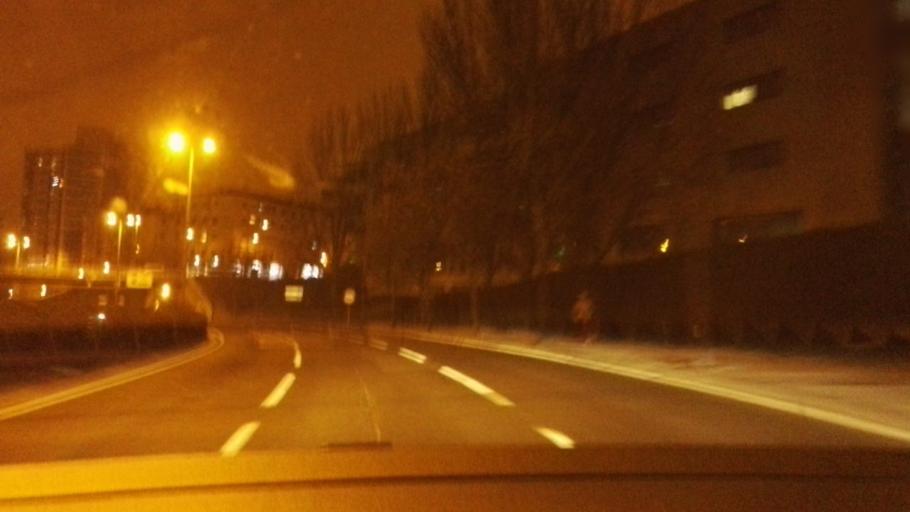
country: ES
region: Navarre
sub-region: Provincia de Navarra
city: Ermitagana
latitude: 42.8140
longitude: -1.6676
